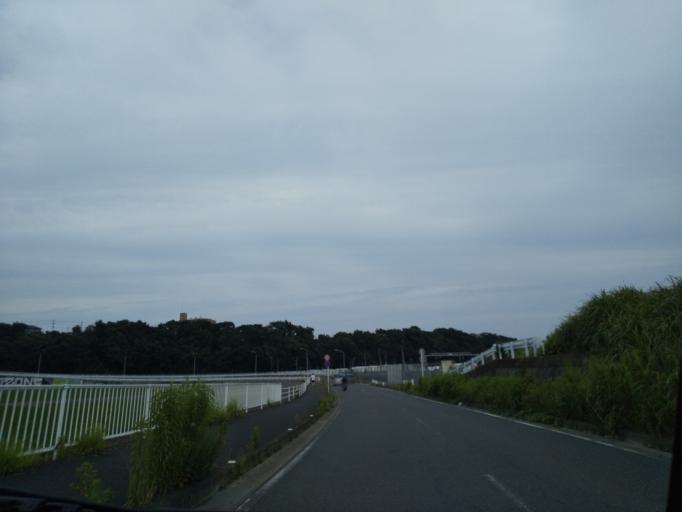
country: JP
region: Kanagawa
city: Zama
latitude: 35.4839
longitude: 139.3590
